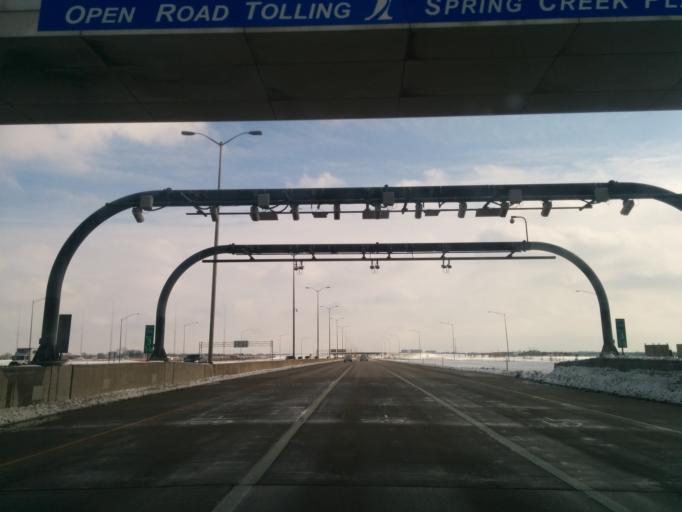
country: US
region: Illinois
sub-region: Will County
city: Lockport
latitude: 41.5773
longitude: -87.9997
